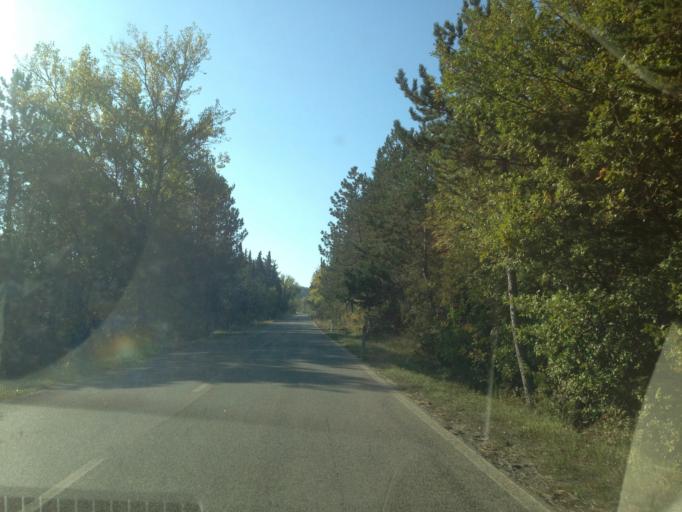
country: IT
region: Tuscany
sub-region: Provincia di Siena
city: Castellina in Chianti
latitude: 43.4873
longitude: 11.2992
